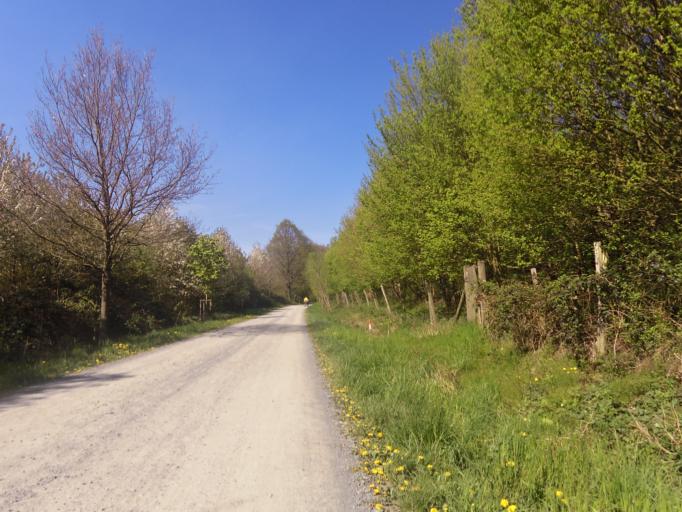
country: DE
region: Hesse
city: Morfelden-Walldorf
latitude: 49.9906
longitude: 8.5917
